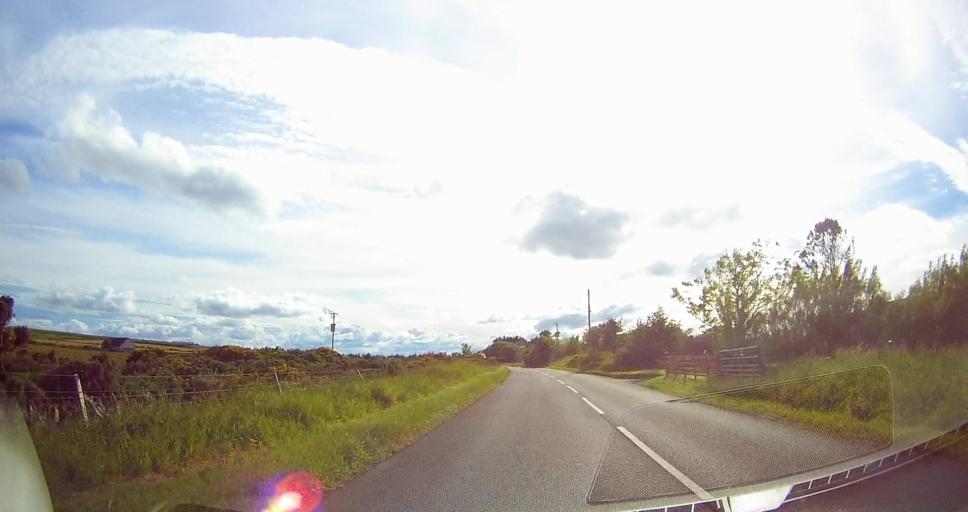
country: GB
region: Scotland
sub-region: Highland
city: Thurso
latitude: 58.6291
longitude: -3.3158
